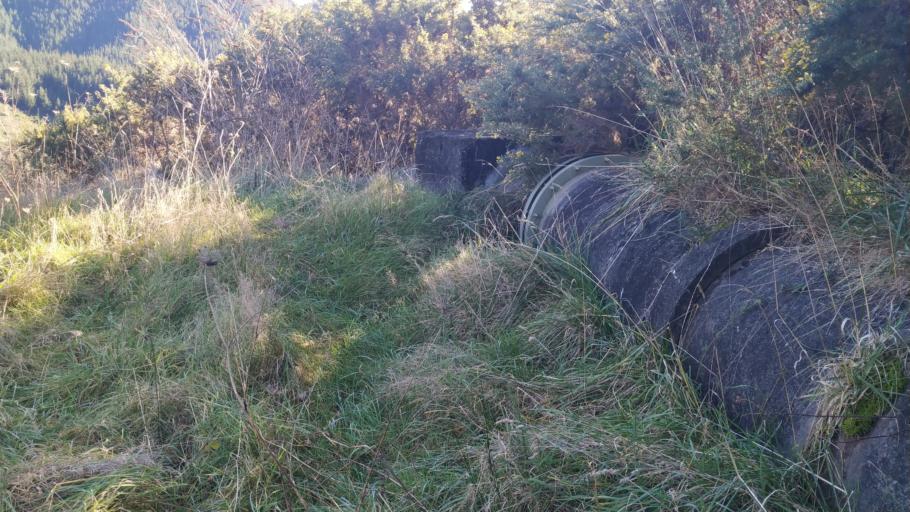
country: NZ
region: Nelson
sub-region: Nelson City
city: Nelson
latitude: -41.2924
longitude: 173.3257
